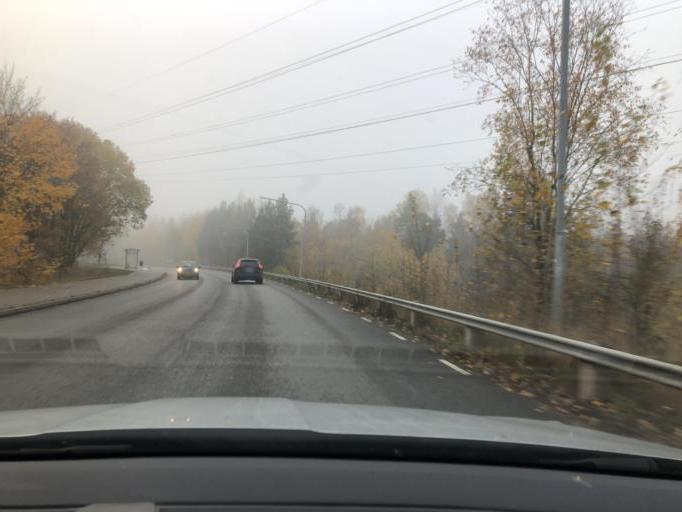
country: SE
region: Stockholm
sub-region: Huddinge Kommun
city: Huddinge
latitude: 59.2245
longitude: 17.9485
